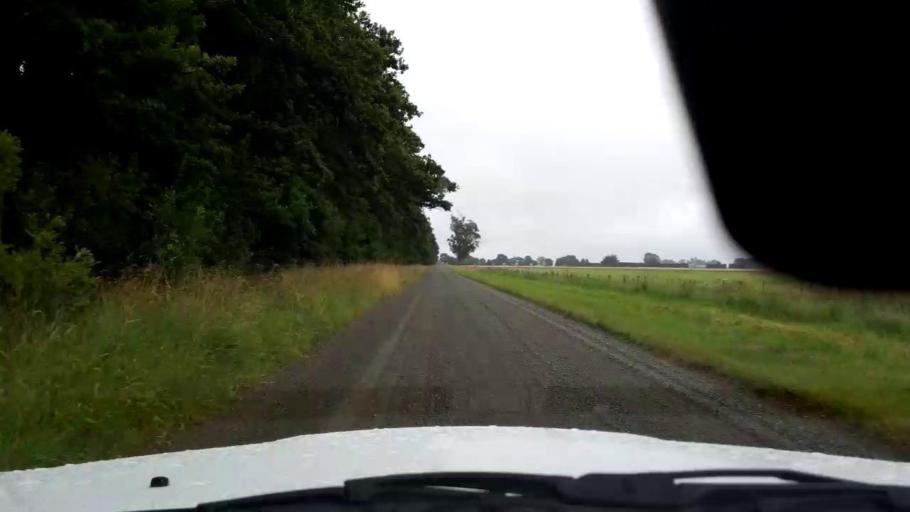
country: NZ
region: Canterbury
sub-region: Timaru District
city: Pleasant Point
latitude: -44.2076
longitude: 171.2814
